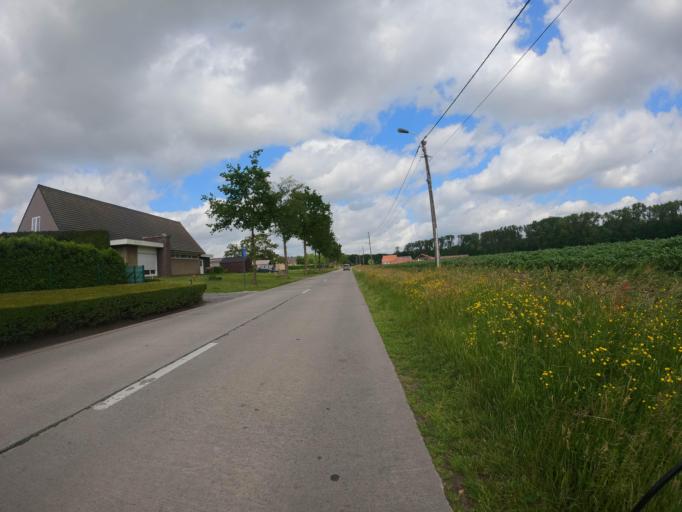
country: BE
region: Flanders
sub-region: Provincie West-Vlaanderen
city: Ruiselede
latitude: 51.0654
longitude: 3.3711
